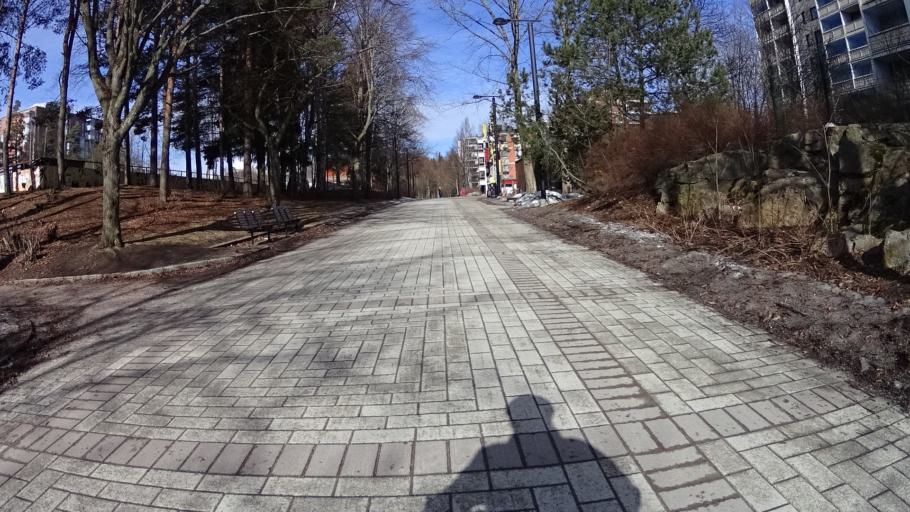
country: FI
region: Uusimaa
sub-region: Helsinki
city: Teekkarikylae
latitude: 60.2677
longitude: 24.8518
